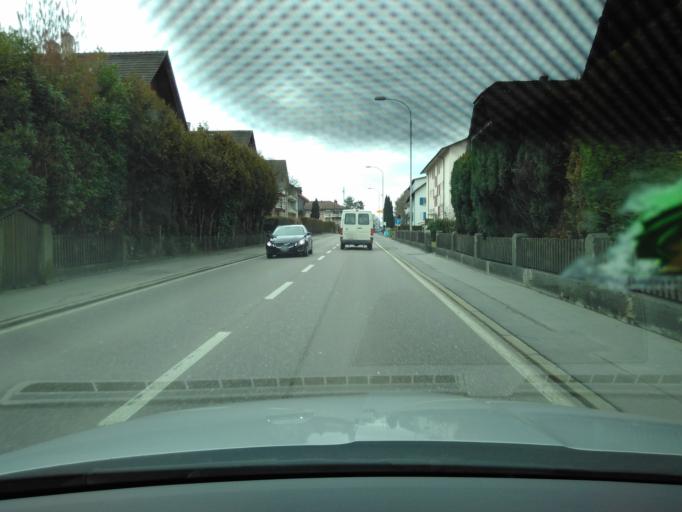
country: CH
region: Lucerne
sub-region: Hochdorf District
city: Emmen
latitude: 47.0858
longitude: 8.2724
